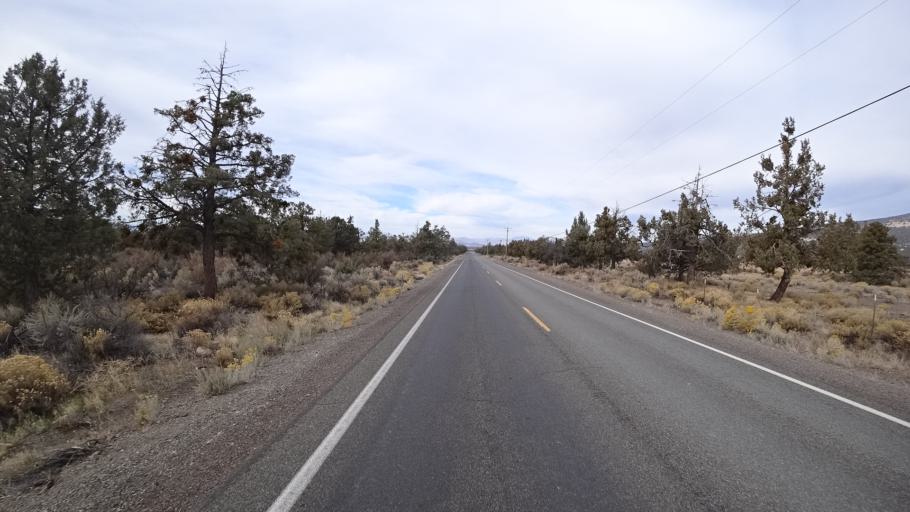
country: US
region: California
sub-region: Siskiyou County
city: Weed
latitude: 41.5829
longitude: -122.2928
